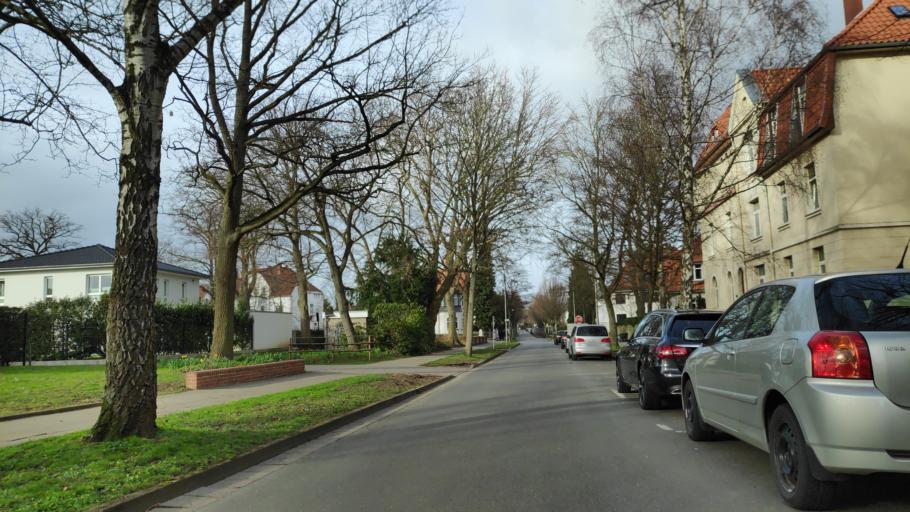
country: DE
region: North Rhine-Westphalia
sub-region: Regierungsbezirk Detmold
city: Minden
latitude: 52.2911
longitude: 8.9056
